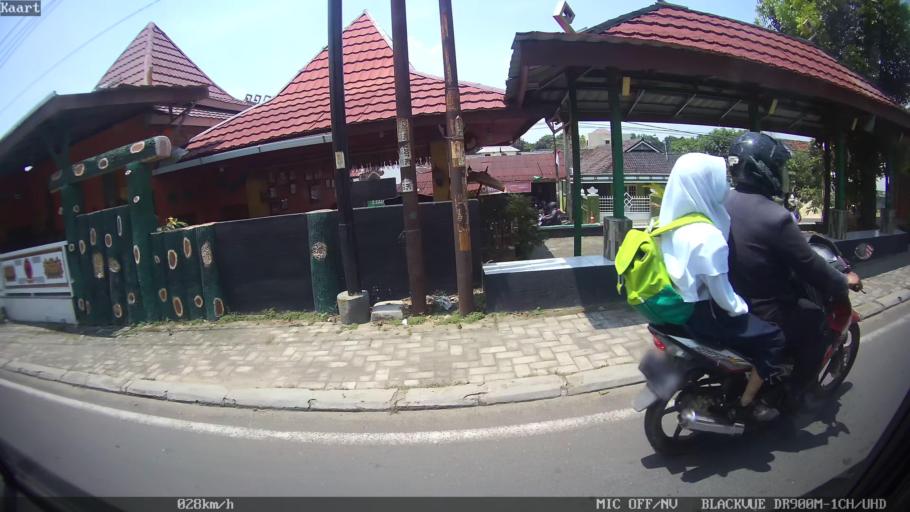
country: ID
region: Lampung
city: Kedaton
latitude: -5.3681
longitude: 105.2354
